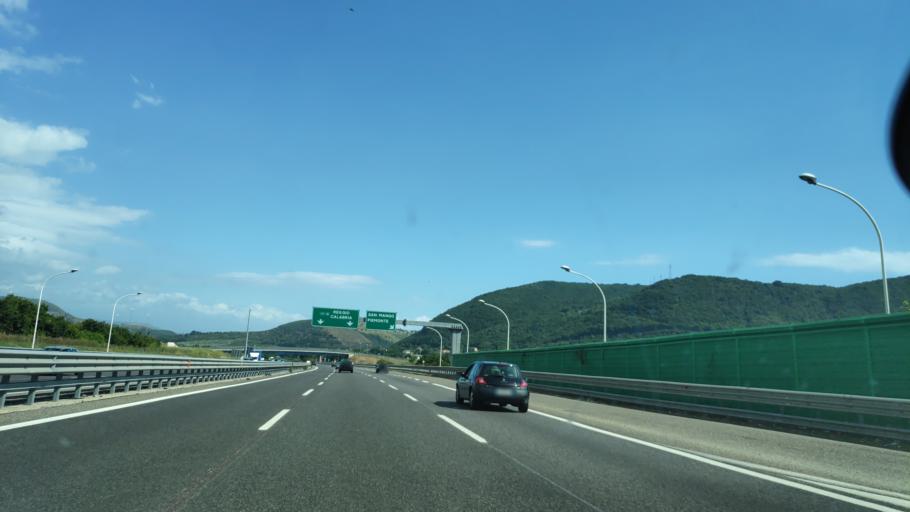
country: IT
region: Campania
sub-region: Provincia di Salerno
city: San Mango Piemonte
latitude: 40.6921
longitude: 14.8355
